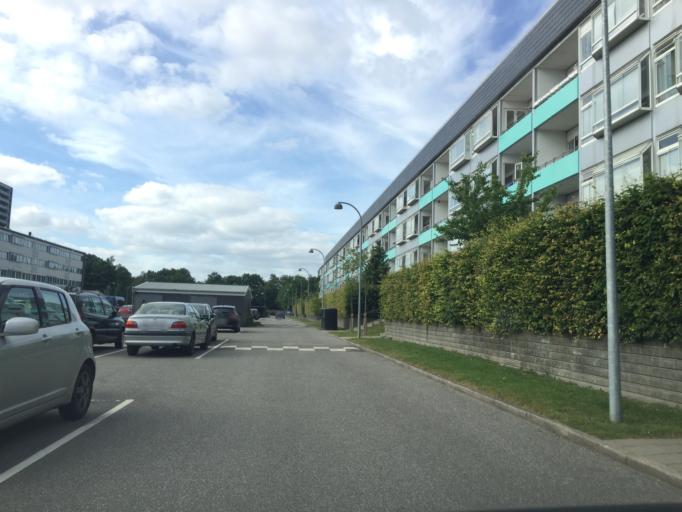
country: DK
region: Capital Region
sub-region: Brondby Kommune
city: Brondbyvester
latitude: 55.6662
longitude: 12.4302
